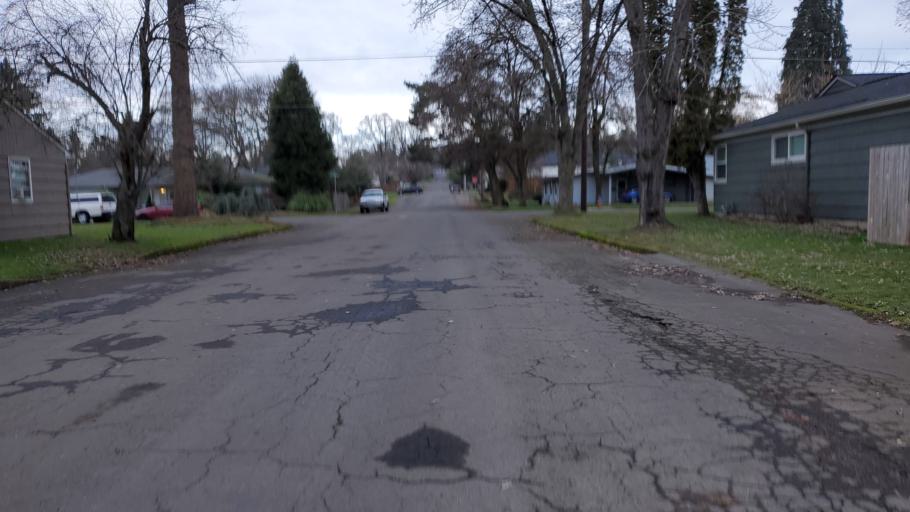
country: US
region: Oregon
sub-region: Clackamas County
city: Gladstone
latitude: 45.3820
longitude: -122.5858
